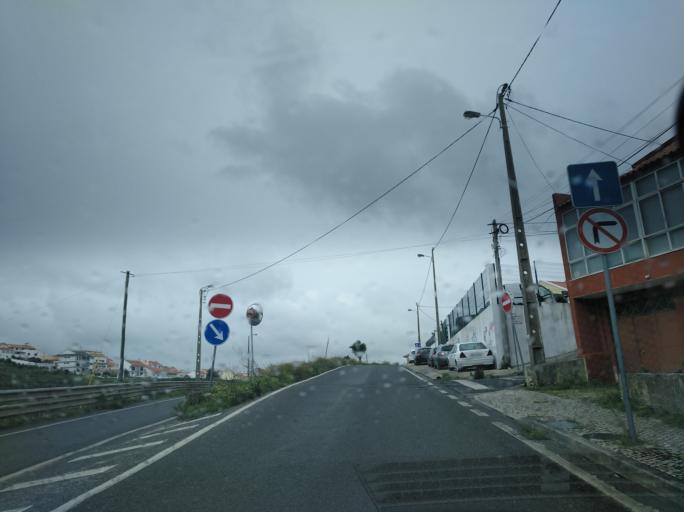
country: PT
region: Lisbon
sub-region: Odivelas
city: Famoes
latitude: 38.7935
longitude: -9.2290
